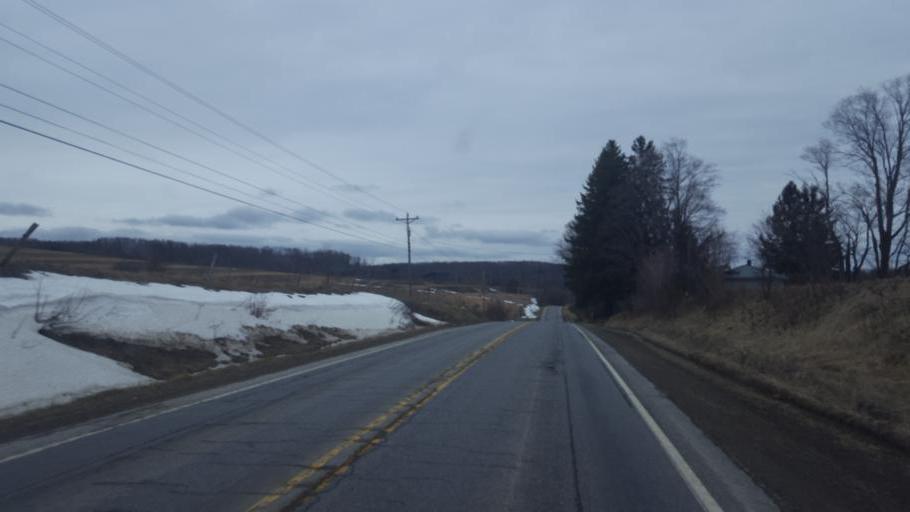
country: US
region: Pennsylvania
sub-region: Potter County
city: Coudersport
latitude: 41.8487
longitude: -77.8841
